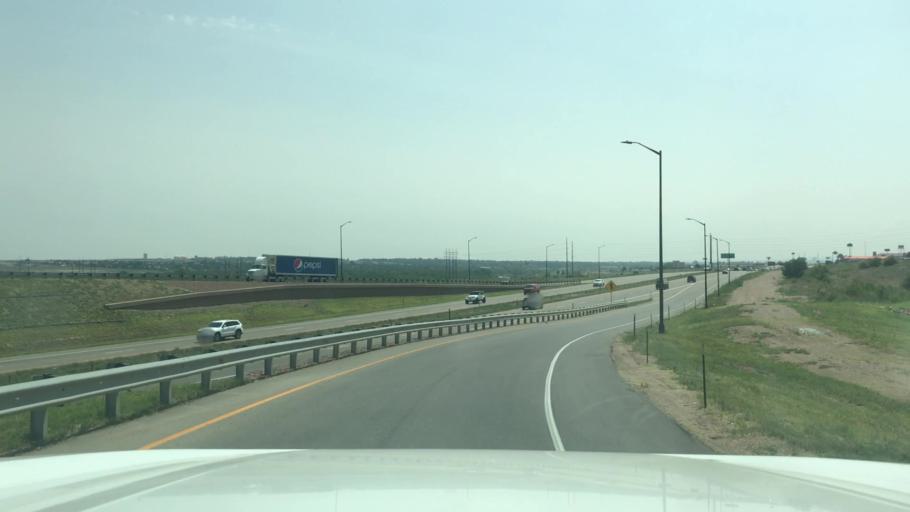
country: US
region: Colorado
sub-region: Pueblo County
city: Pueblo
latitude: 38.3370
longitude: -104.6200
